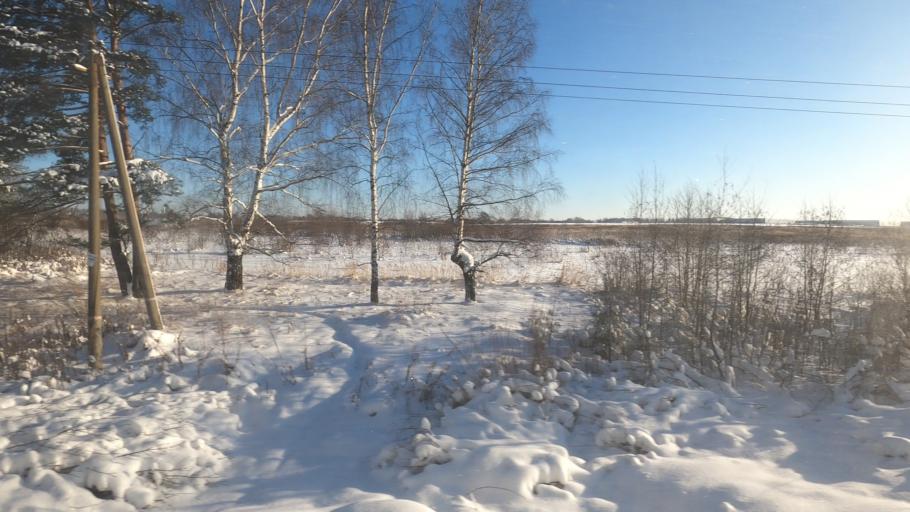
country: RU
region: Moskovskaya
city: Orud'yevo
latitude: 56.4316
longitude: 37.5011
